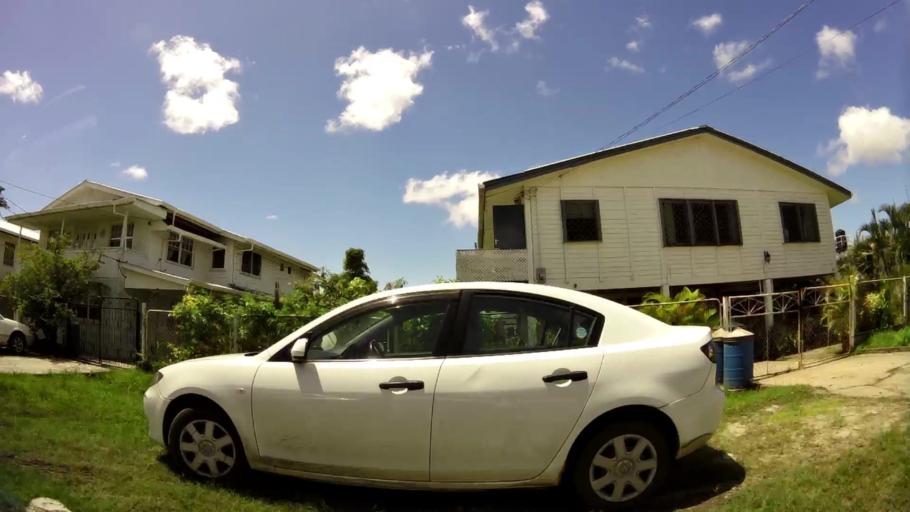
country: GY
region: Demerara-Mahaica
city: Georgetown
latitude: 6.7862
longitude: -58.1491
